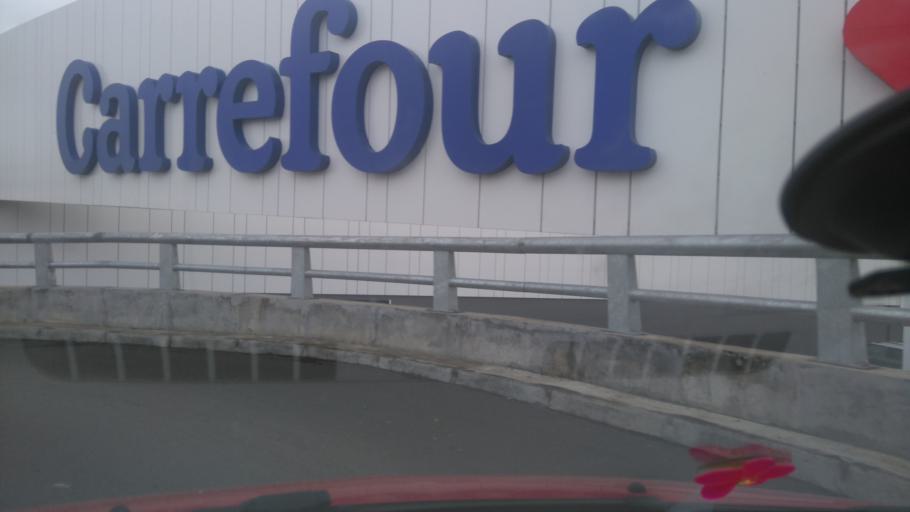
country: MQ
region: Martinique
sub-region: Martinique
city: Ducos
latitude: 14.5557
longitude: -60.9736
